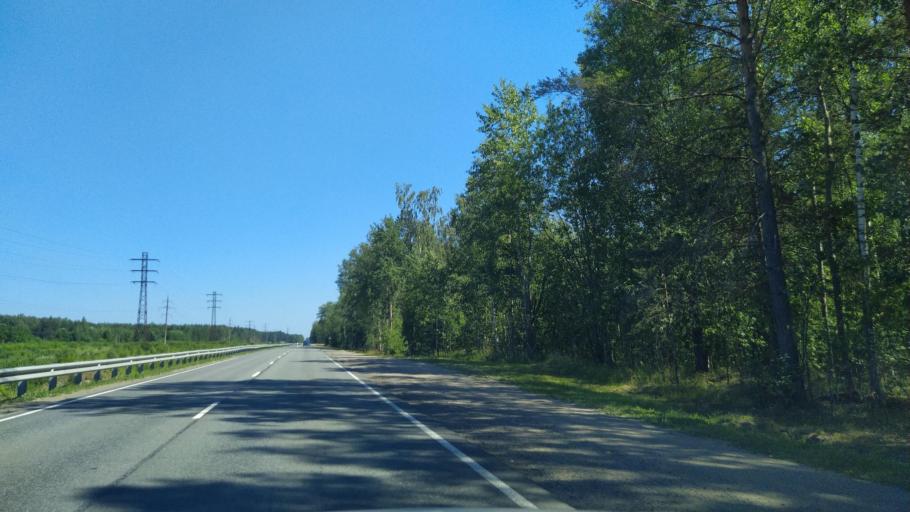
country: RU
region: Leningrad
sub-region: Volosovskiy Rayon
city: Shlissel'burg
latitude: 59.9525
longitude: 30.9927
